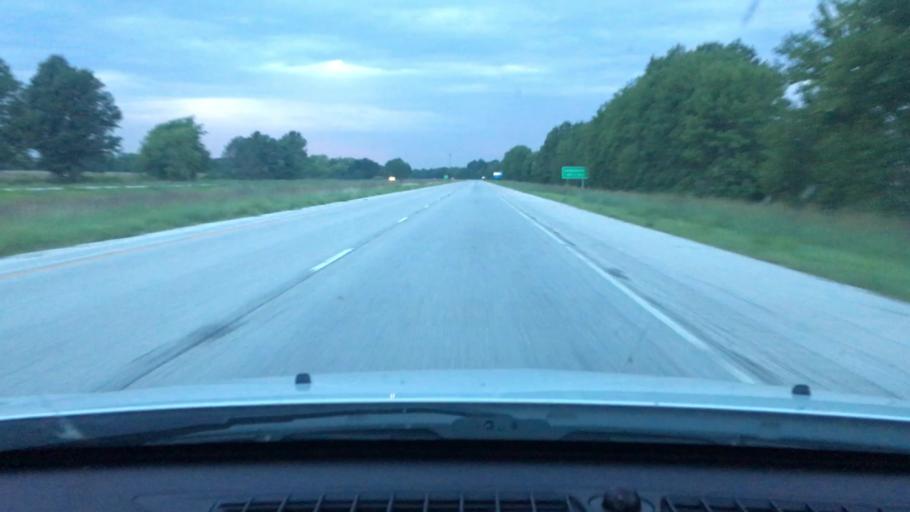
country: US
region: Illinois
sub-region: Morgan County
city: Jacksonville
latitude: 39.7379
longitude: -90.1375
